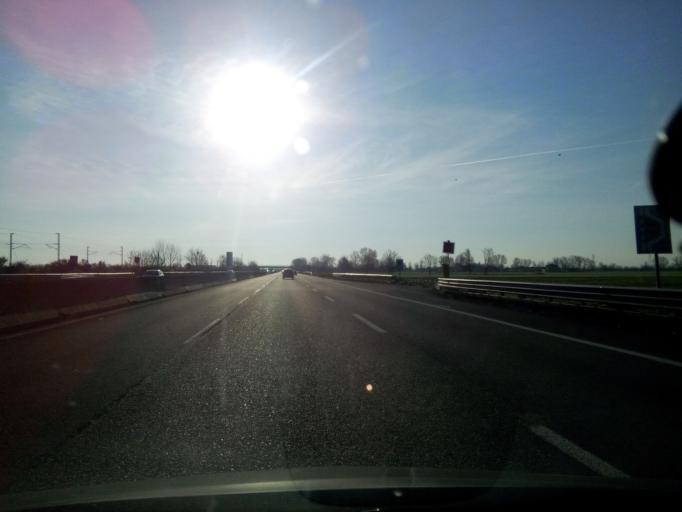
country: IT
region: Emilia-Romagna
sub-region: Provincia di Parma
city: Fontanellato
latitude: 44.8802
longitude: 10.1483
